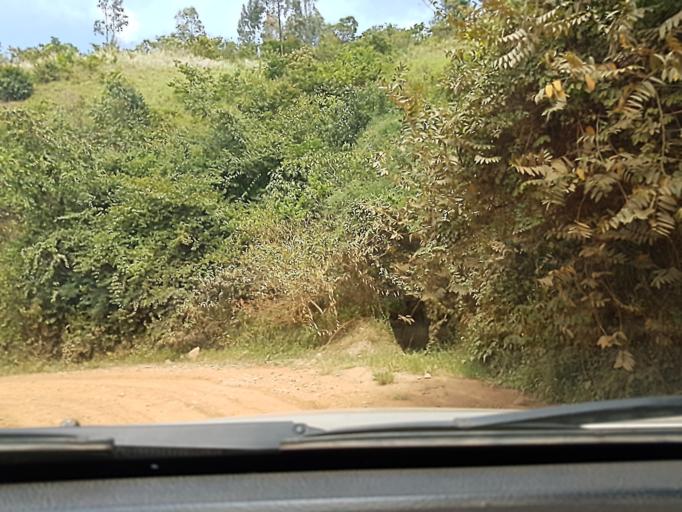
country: RW
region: Western Province
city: Cyangugu
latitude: -2.7046
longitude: 28.9501
